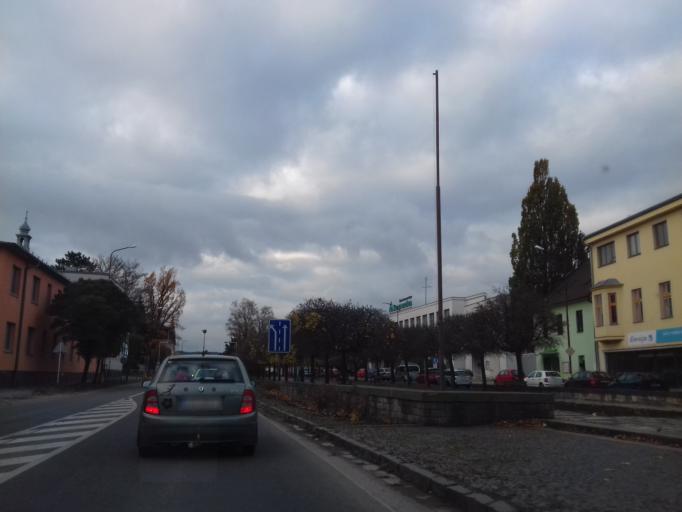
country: CZ
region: Pardubicky
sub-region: Okres Svitavy
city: Svitavy
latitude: 49.7570
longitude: 16.4645
